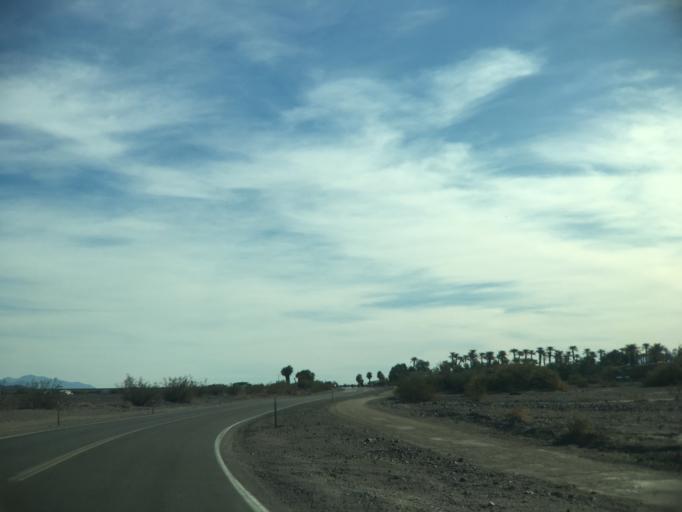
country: US
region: Nevada
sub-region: Nye County
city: Beatty
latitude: 36.4653
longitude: -116.8658
